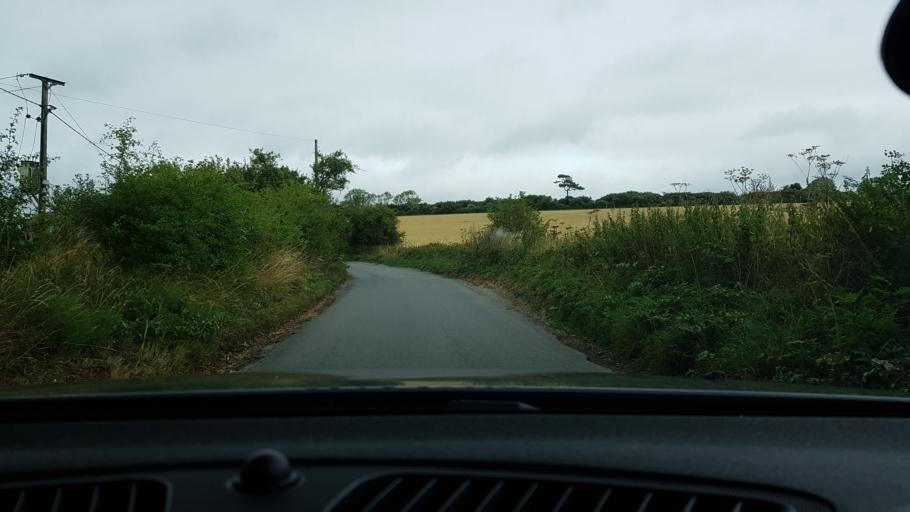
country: GB
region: England
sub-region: Wiltshire
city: Shalbourne
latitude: 51.3715
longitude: -1.5319
